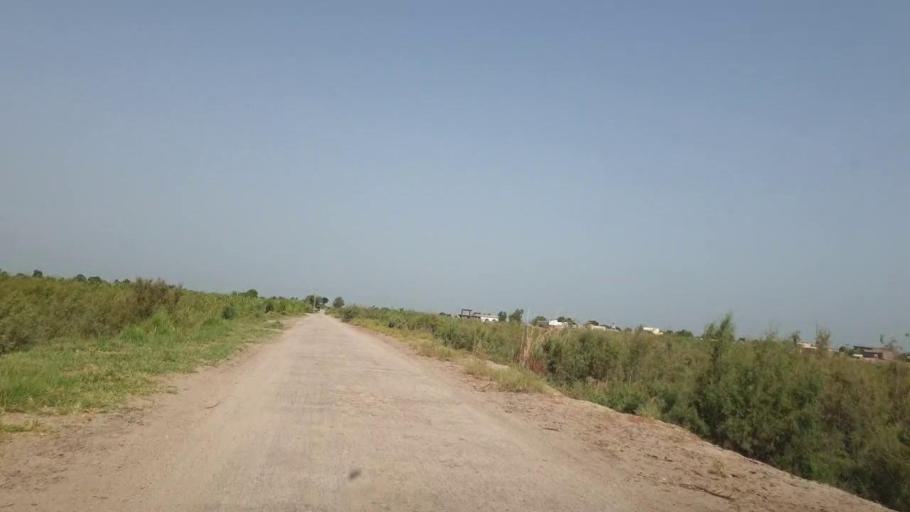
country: PK
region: Sindh
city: Sakrand
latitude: 26.3055
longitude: 68.2174
